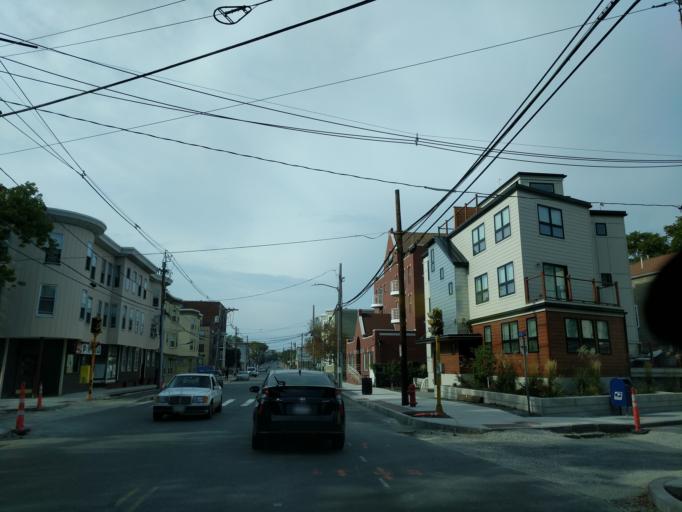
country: US
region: Massachusetts
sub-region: Middlesex County
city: Cambridge
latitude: 42.3819
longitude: -71.1108
